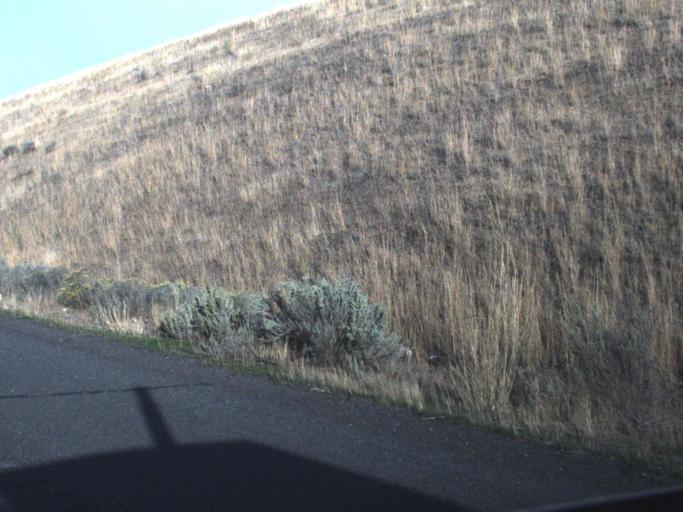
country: US
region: Oregon
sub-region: Umatilla County
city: Umatilla
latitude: 45.9759
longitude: -119.3335
